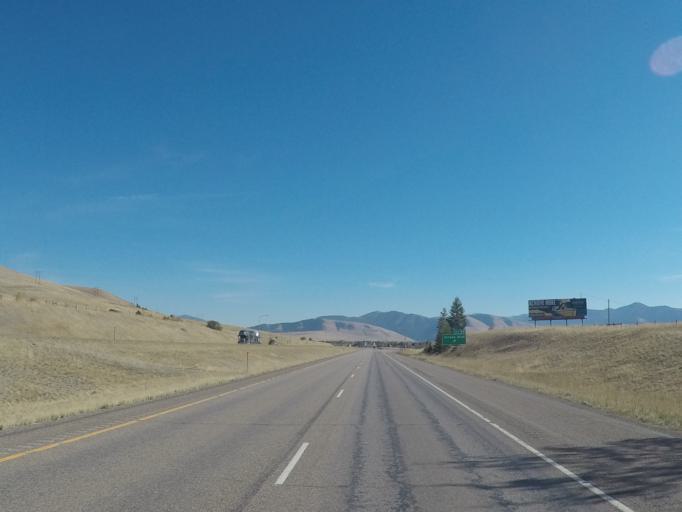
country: US
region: Montana
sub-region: Missoula County
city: Orchard Homes
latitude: 46.9268
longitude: -114.0756
